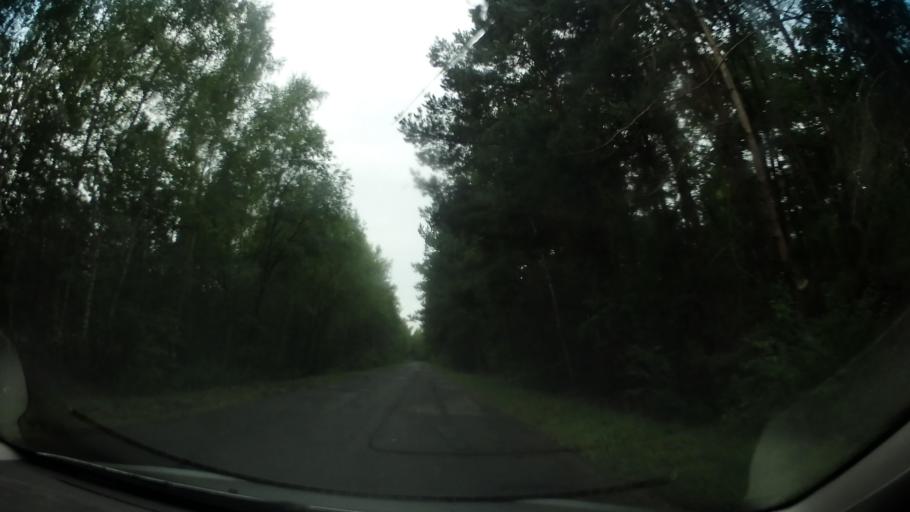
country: CZ
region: Central Bohemia
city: Milovice
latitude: 50.2437
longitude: 14.9027
